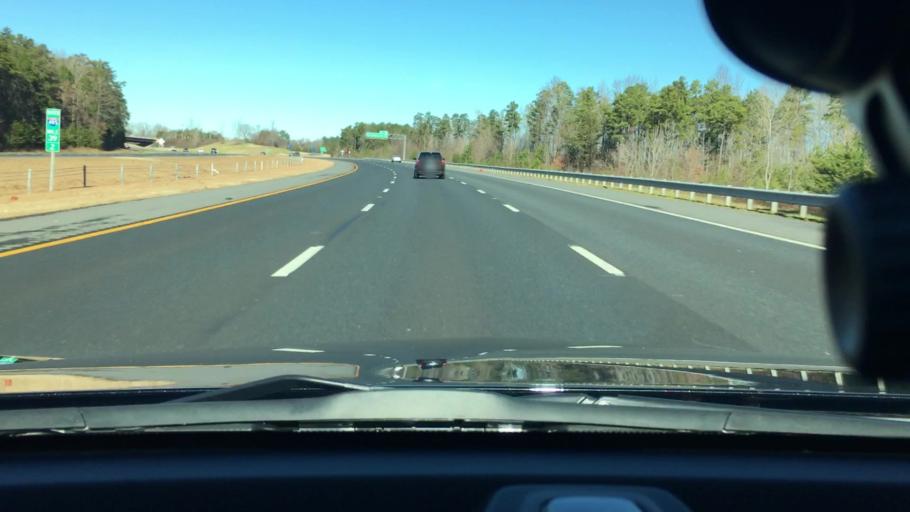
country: US
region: North Carolina
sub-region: Mecklenburg County
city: Mint Hill
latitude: 35.2477
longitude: -80.6499
